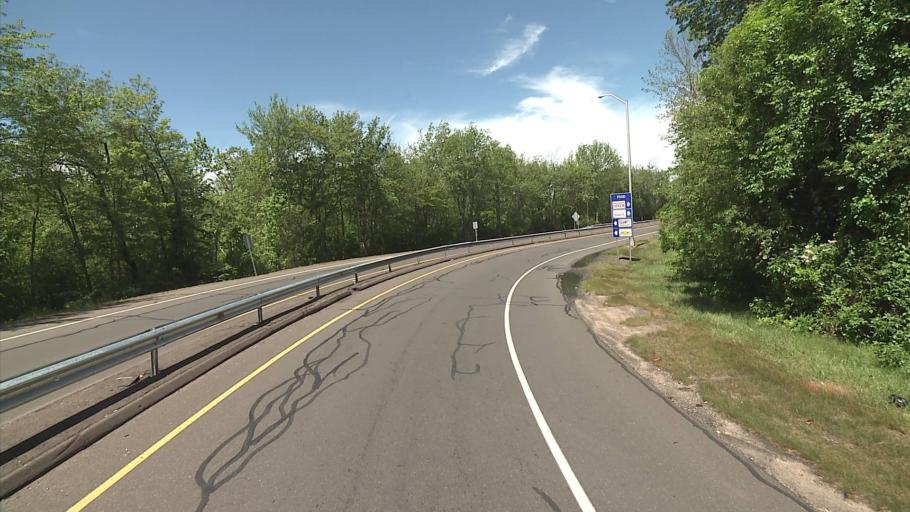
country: US
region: Connecticut
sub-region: New Haven County
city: Branford
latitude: 41.2919
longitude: -72.7812
